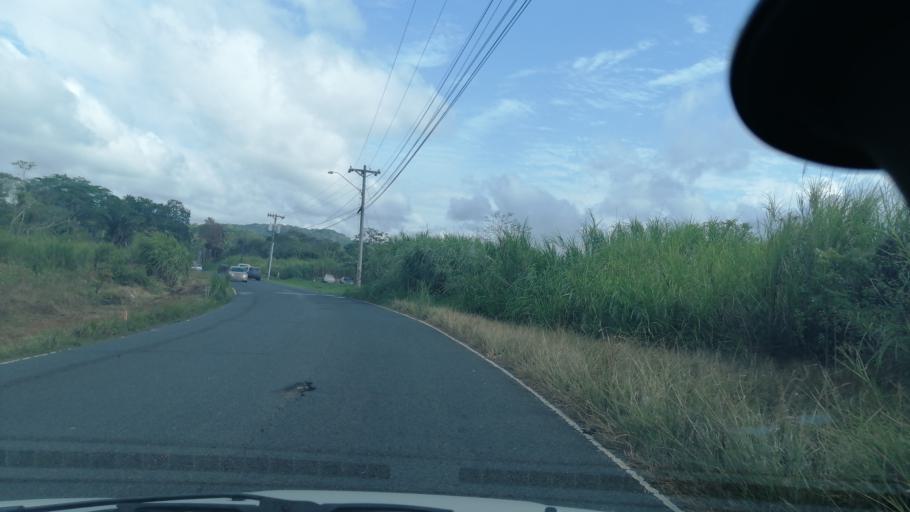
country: PA
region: Panama
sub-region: Distrito de Panama
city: Paraiso
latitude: 9.0507
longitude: -79.6368
